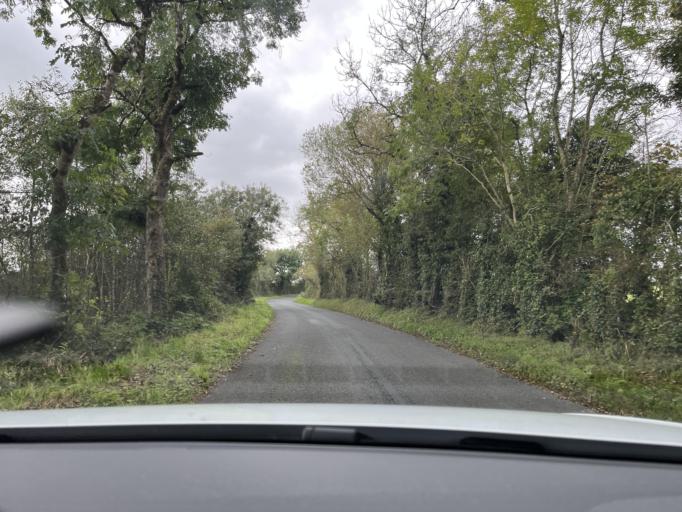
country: IE
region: Connaught
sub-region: County Leitrim
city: Carrick-on-Shannon
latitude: 53.9666
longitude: -8.0921
